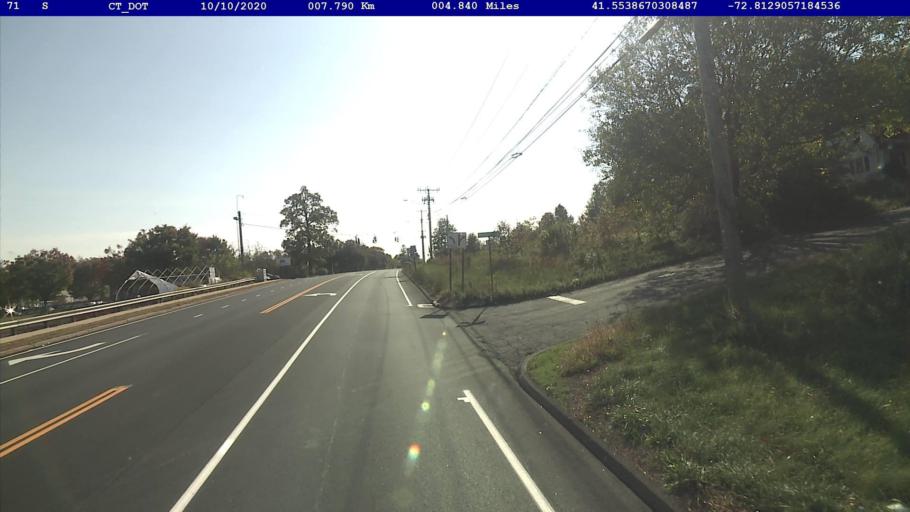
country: US
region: Connecticut
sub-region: New Haven County
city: Meriden
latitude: 41.5539
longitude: -72.8129
